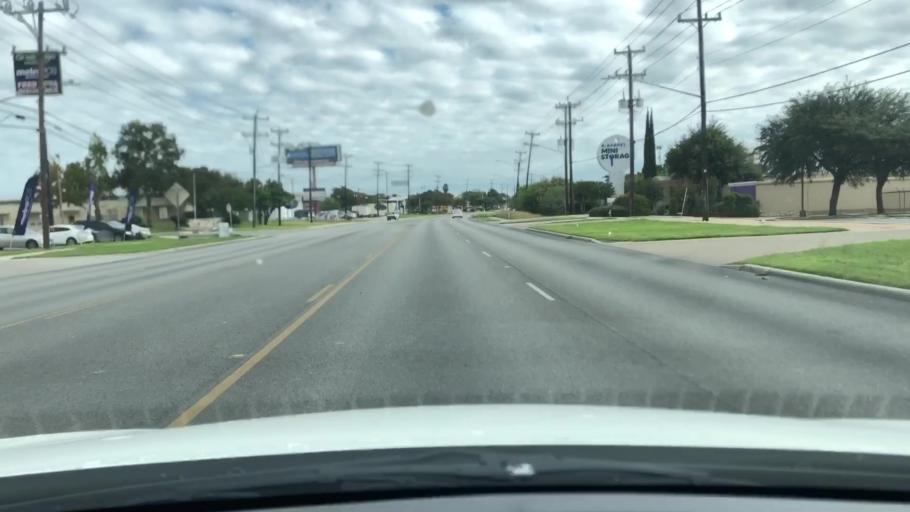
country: US
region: Texas
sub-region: Bexar County
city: Leon Valley
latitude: 29.4835
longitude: -98.6644
